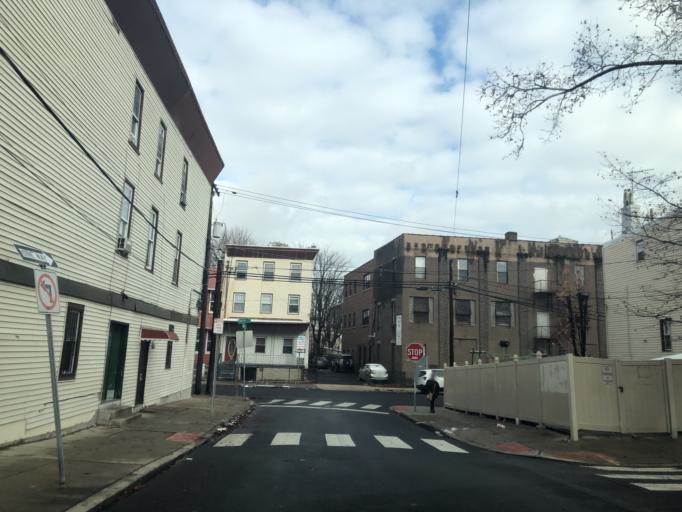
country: US
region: New Jersey
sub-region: Hudson County
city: Hoboken
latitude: 40.7408
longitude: -74.0501
